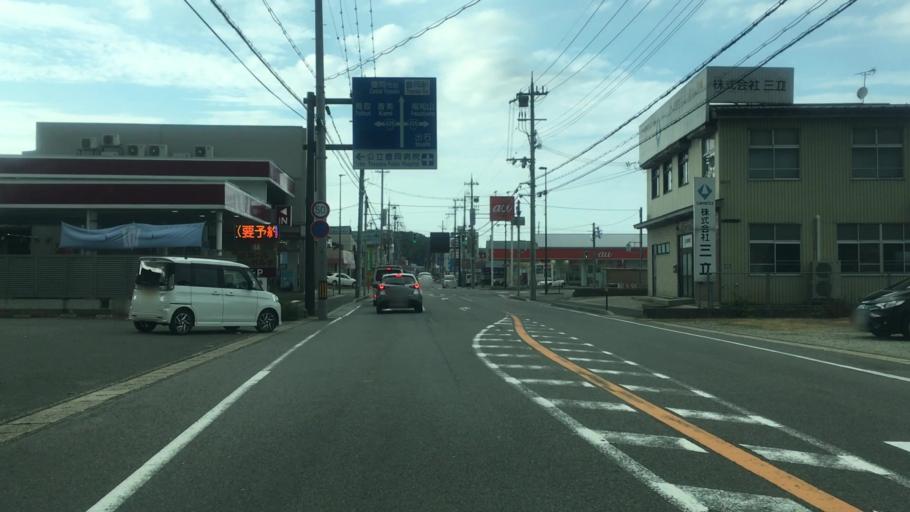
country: JP
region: Hyogo
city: Toyooka
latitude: 35.5274
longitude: 134.8207
